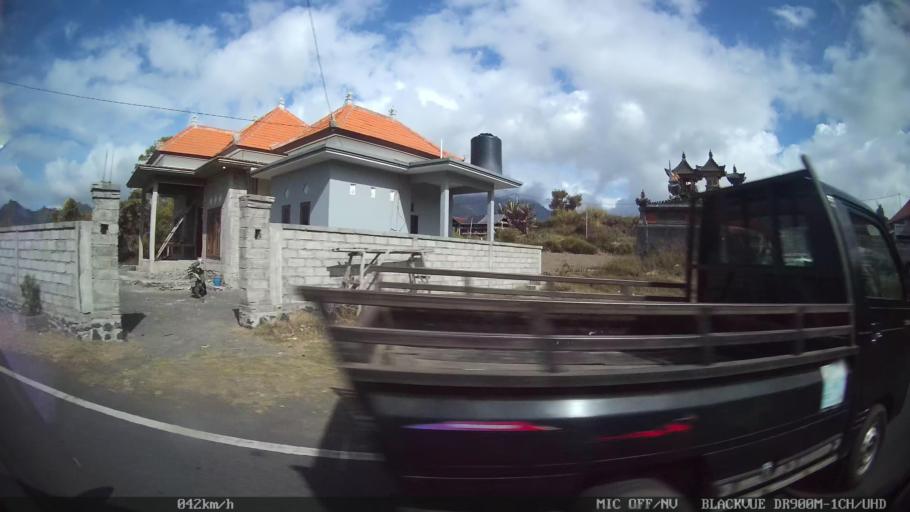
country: ID
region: Bali
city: Banjar Trunyan
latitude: -8.2431
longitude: 115.4018
